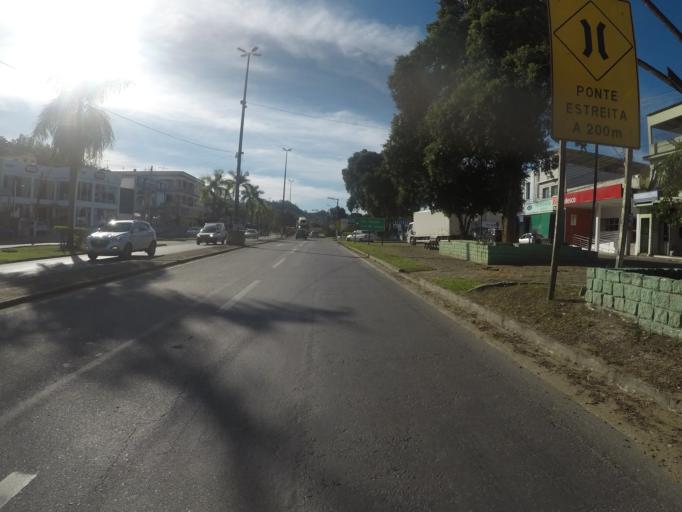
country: BR
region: Espirito Santo
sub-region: Fundao
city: Fundao
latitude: -19.9333
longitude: -40.4049
